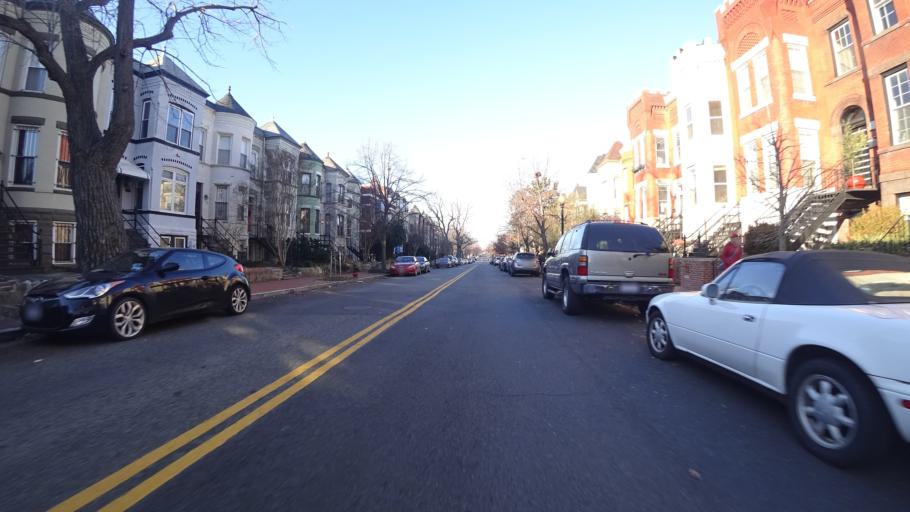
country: US
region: Washington, D.C.
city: Washington, D.C.
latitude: 38.9126
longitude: -77.0103
